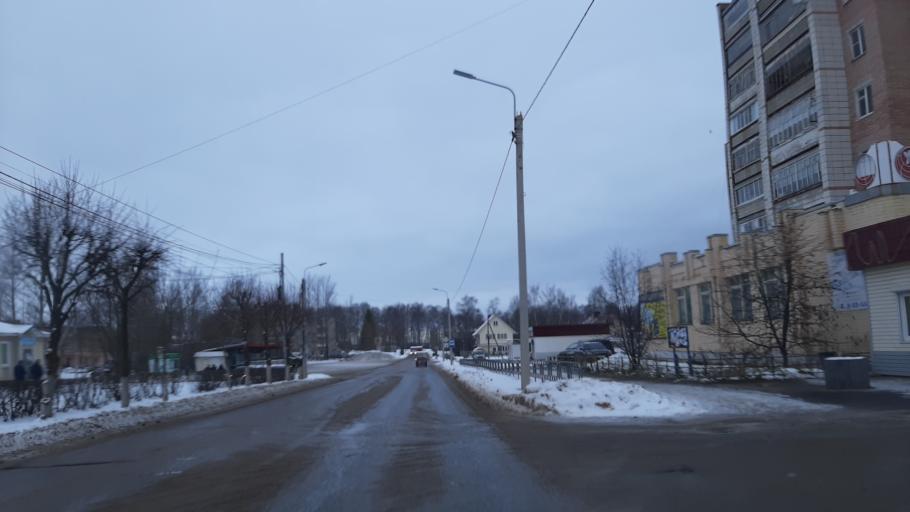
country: RU
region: Kostroma
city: Volgorechensk
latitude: 57.4427
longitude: 41.1491
